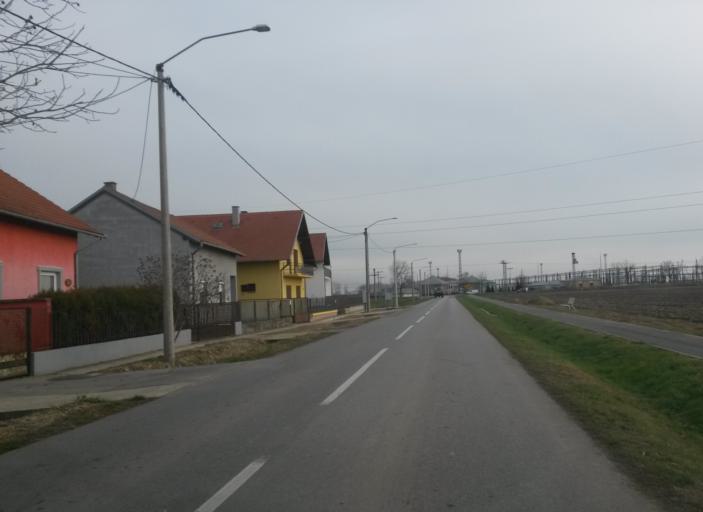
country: HR
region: Osjecko-Baranjska
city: Antunovac
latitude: 45.4759
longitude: 18.6585
